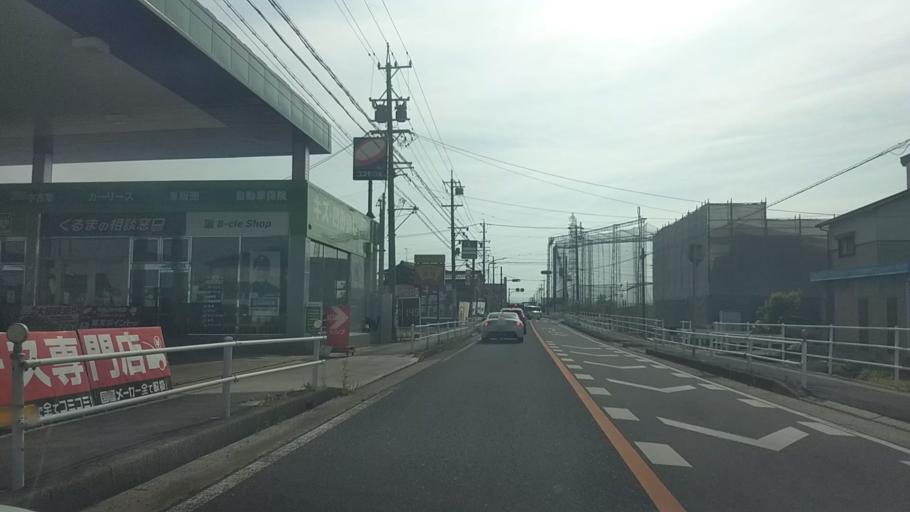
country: JP
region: Aichi
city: Anjo
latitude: 34.9601
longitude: 137.1121
